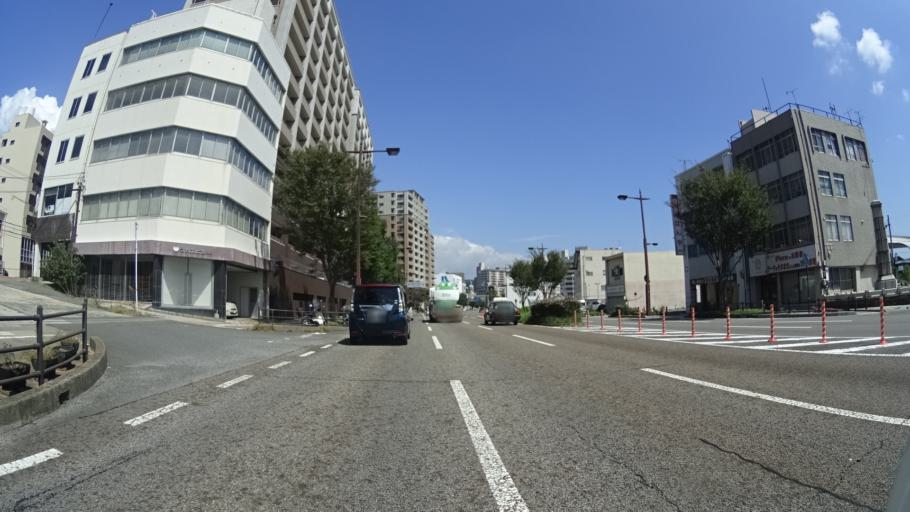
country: JP
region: Yamaguchi
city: Shimonoseki
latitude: 33.9543
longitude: 130.9402
